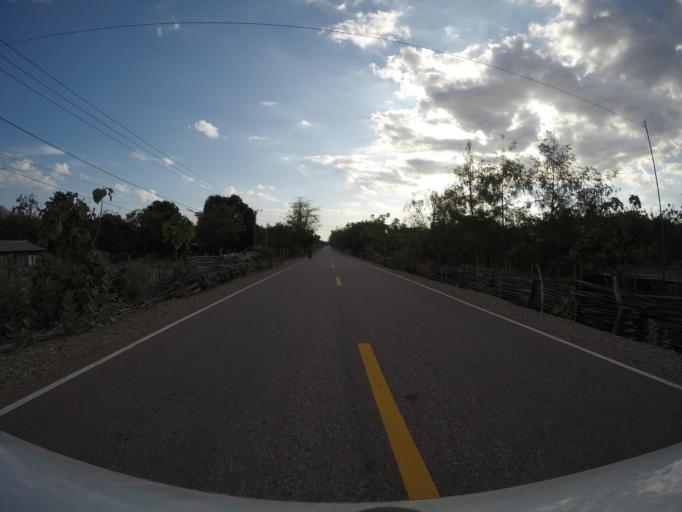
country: TL
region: Bobonaro
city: Maliana
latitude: -8.8902
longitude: 125.0200
